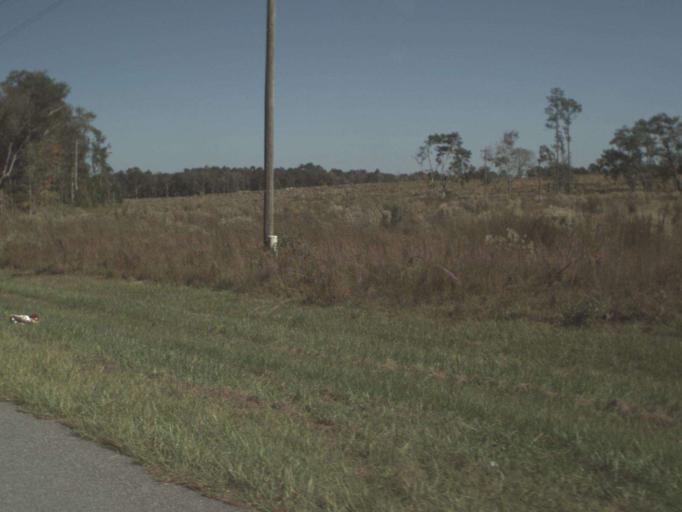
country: US
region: Florida
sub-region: Jefferson County
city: Monticello
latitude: 30.4578
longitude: -84.0190
